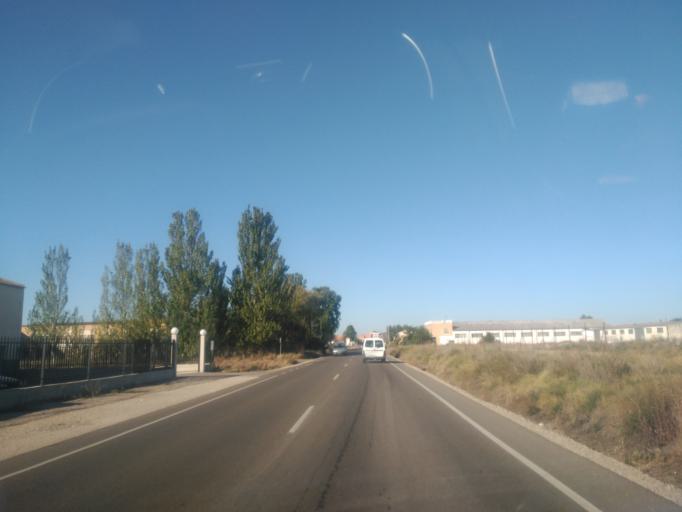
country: ES
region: Castille and Leon
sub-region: Provincia de Burgos
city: Aranda de Duero
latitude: 41.6751
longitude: -3.6654
